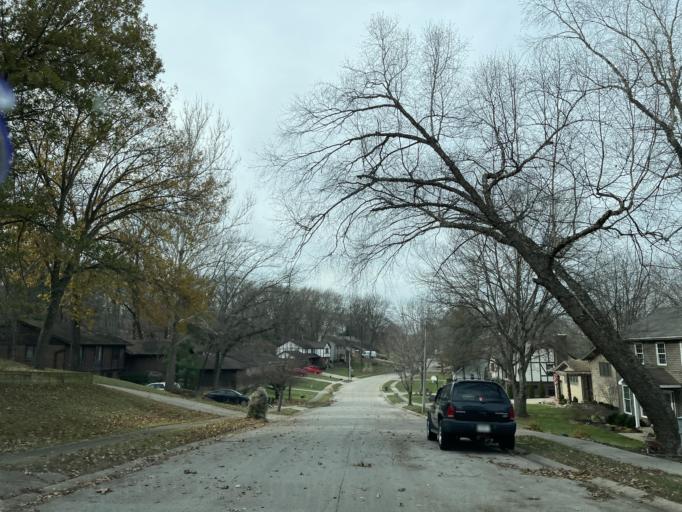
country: US
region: Illinois
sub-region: Sangamon County
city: Leland Grove
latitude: 39.8089
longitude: -89.7243
